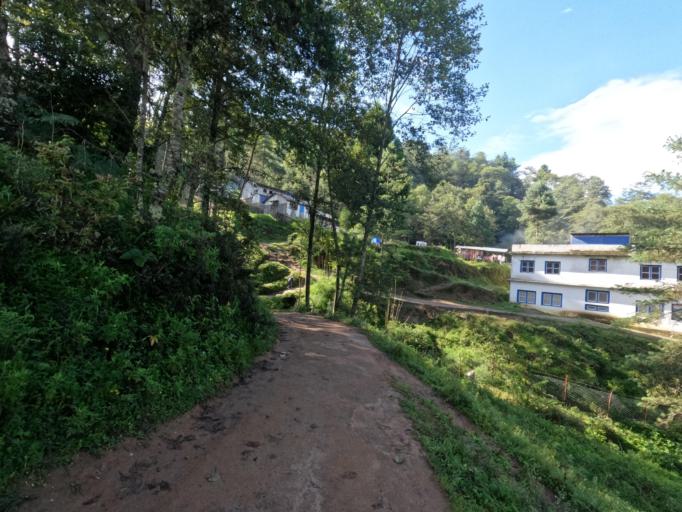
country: NP
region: Eastern Region
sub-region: Sagarmatha Zone
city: Namche Bazar
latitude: 27.4944
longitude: 86.5838
